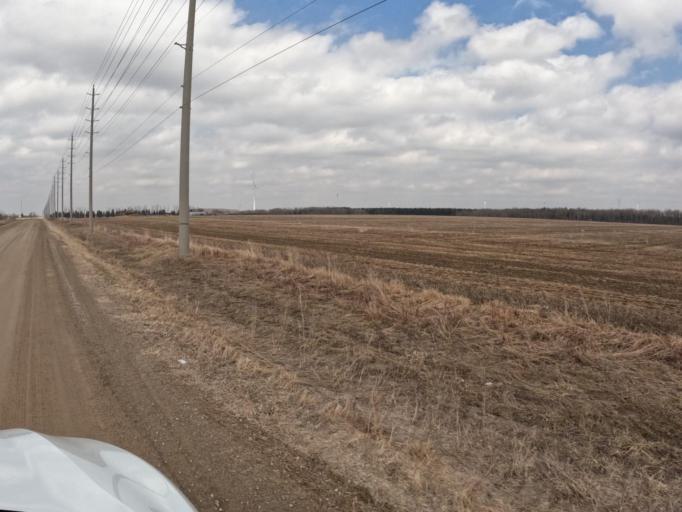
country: CA
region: Ontario
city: Shelburne
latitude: 44.0292
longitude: -80.3149
